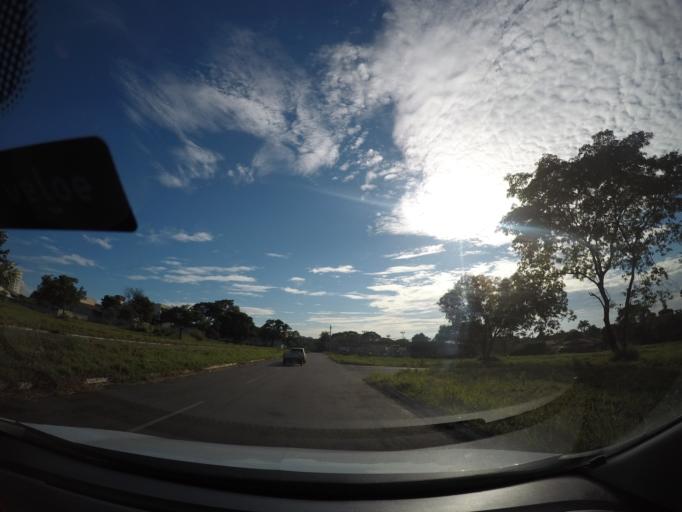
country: BR
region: Goias
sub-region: Goiania
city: Goiania
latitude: -16.7456
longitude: -49.2717
